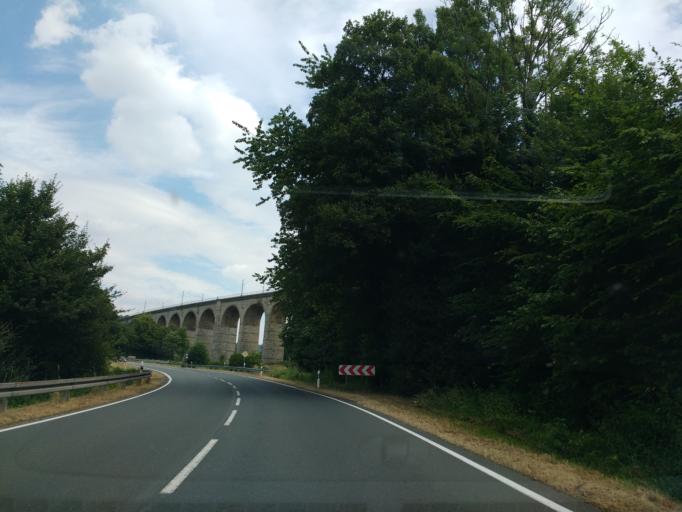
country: DE
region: North Rhine-Westphalia
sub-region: Regierungsbezirk Detmold
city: Altenbeken
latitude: 51.7615
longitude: 8.9224
